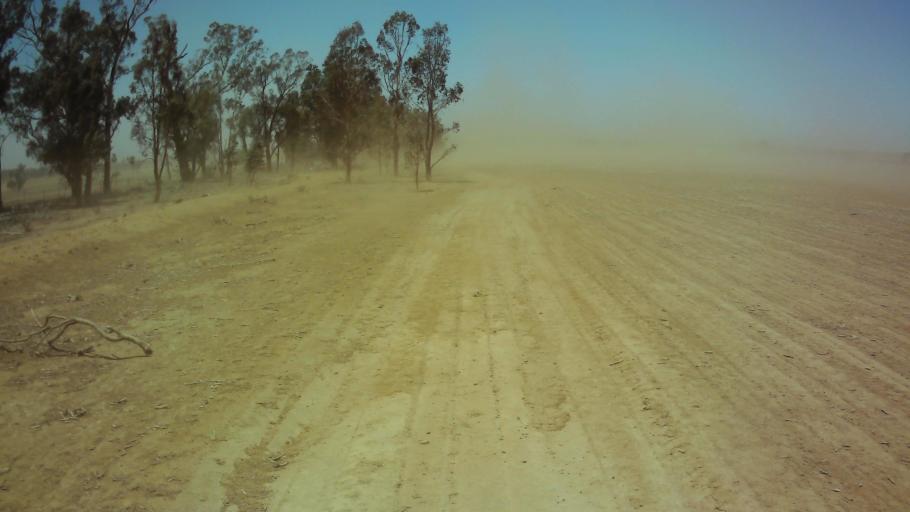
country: AU
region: New South Wales
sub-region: Forbes
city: Forbes
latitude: -33.7131
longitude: 147.7828
